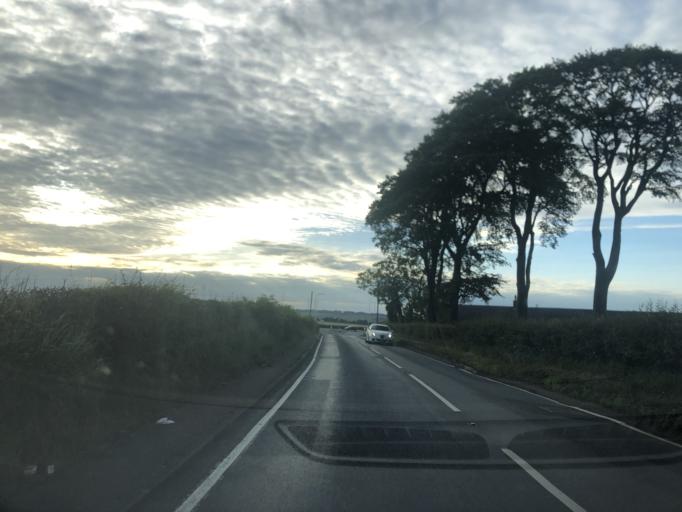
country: GB
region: Scotland
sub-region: Fife
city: East Wemyss
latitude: 56.1812
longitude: -3.0547
